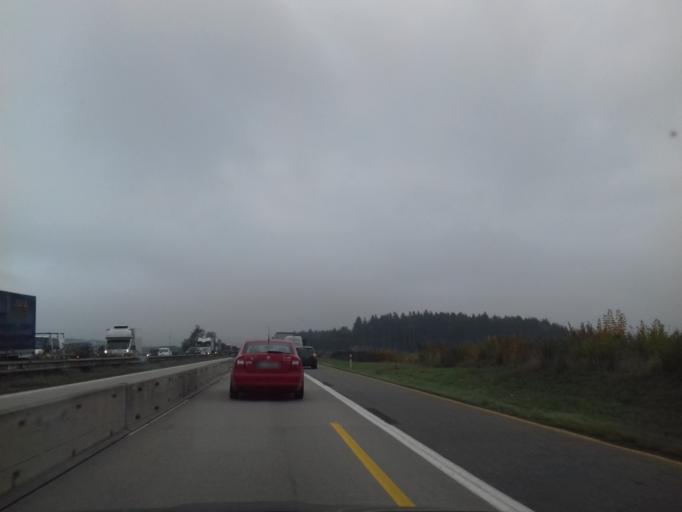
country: CZ
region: Vysocina
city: Dobronin
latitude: 49.4389
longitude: 15.6390
